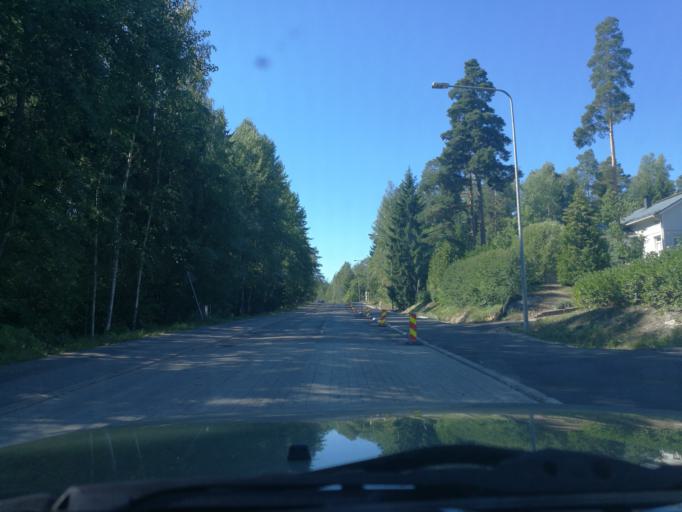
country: FI
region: Uusimaa
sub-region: Helsinki
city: Kerava
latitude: 60.3453
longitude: 25.1168
